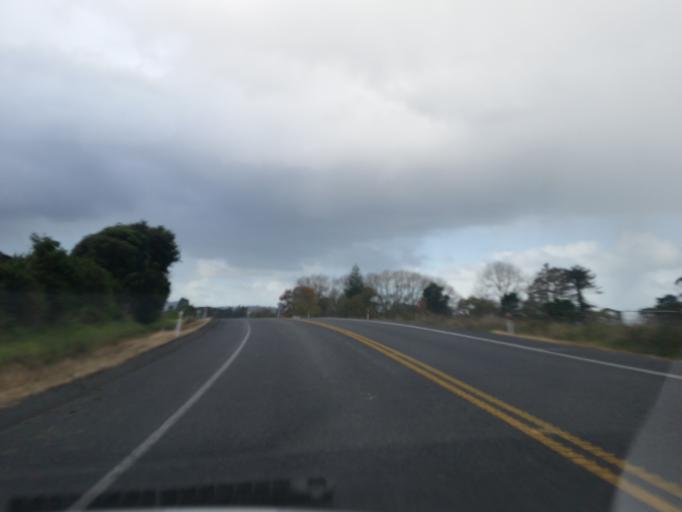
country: NZ
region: Auckland
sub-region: Auckland
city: Pukekohe East
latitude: -37.2144
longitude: 175.0684
